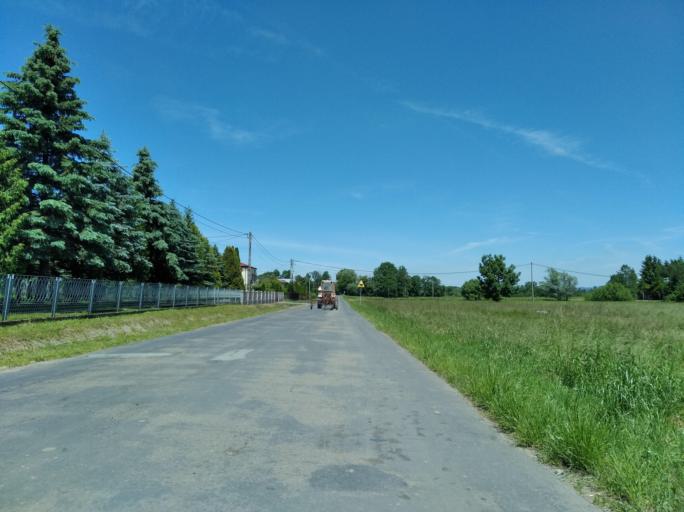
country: PL
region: Subcarpathian Voivodeship
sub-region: Powiat jasielski
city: Tarnowiec
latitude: 49.7001
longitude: 21.5528
